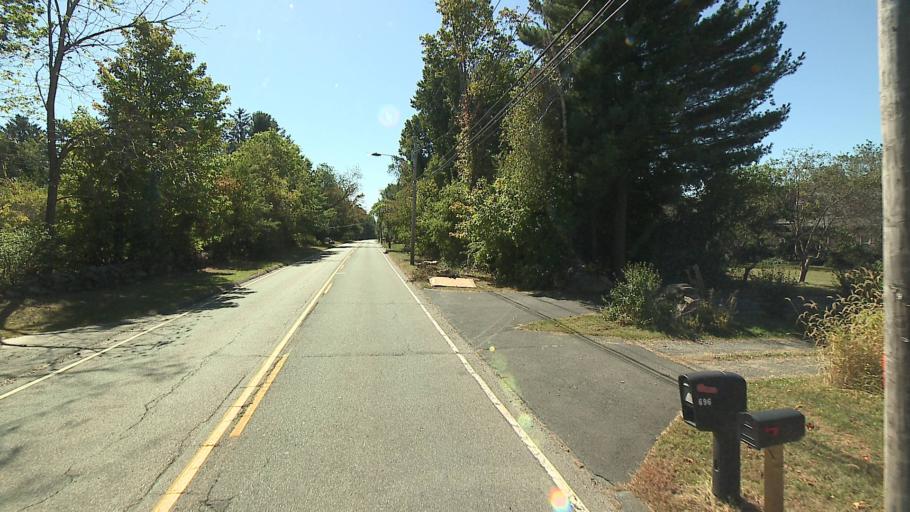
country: US
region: Connecticut
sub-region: New Haven County
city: City of Milford (balance)
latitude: 41.2487
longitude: -73.0531
